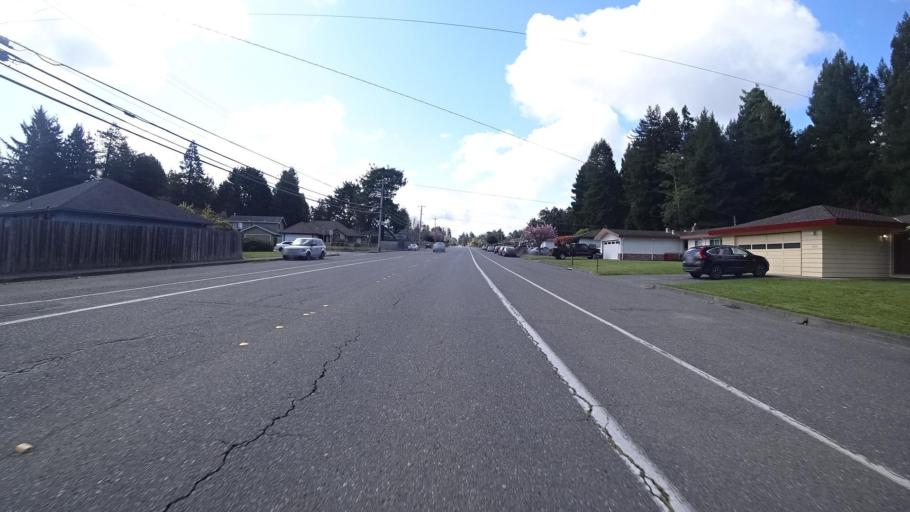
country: US
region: California
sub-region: Humboldt County
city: Pine Hills
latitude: 40.7437
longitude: -124.1474
